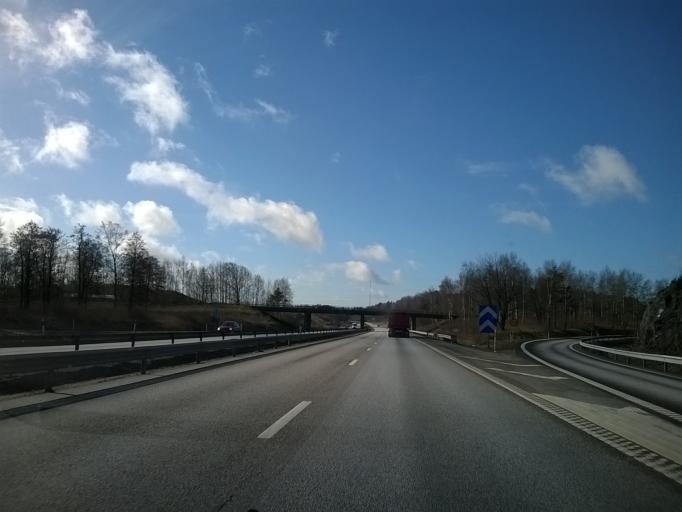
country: SE
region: Halland
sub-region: Kungsbacka Kommun
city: Kungsbacka
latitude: 57.4901
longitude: 12.0466
